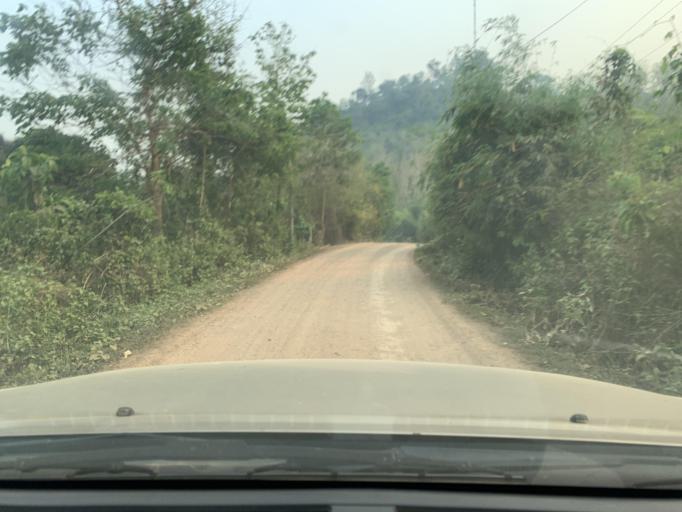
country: LA
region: Louangphabang
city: Louangphabang
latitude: 19.9241
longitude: 102.0743
